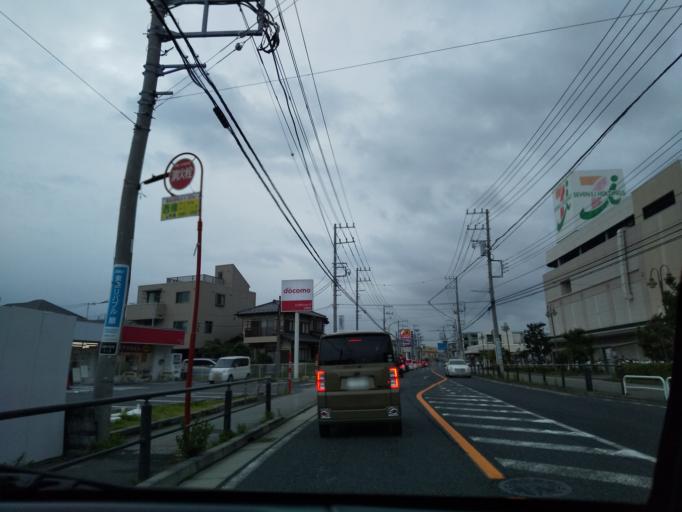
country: JP
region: Kanagawa
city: Fujisawa
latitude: 35.4128
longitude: 139.4998
